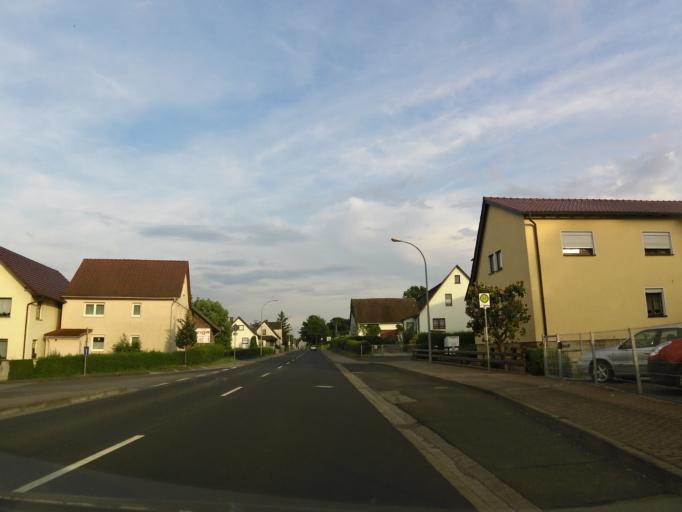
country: DE
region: Thuringia
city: Immelborn
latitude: 50.8019
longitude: 10.2666
